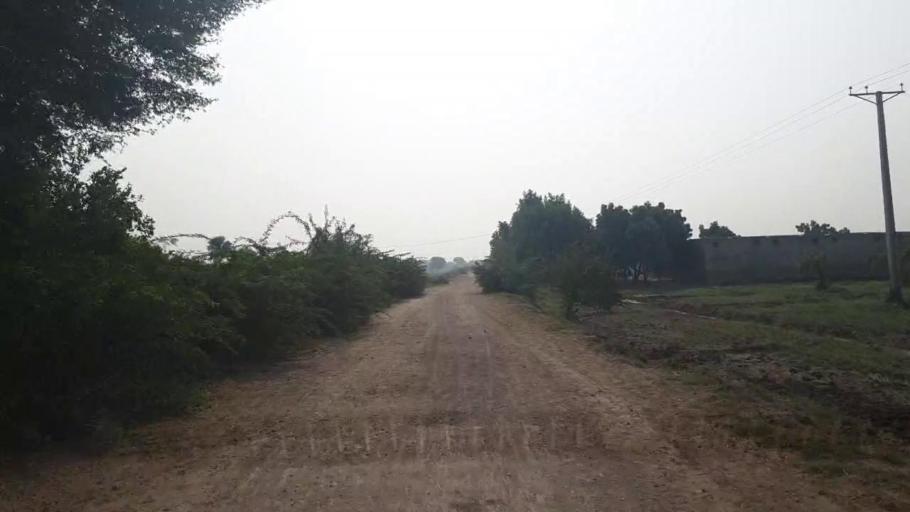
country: PK
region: Sindh
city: Tando Muhammad Khan
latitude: 25.2658
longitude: 68.5106
